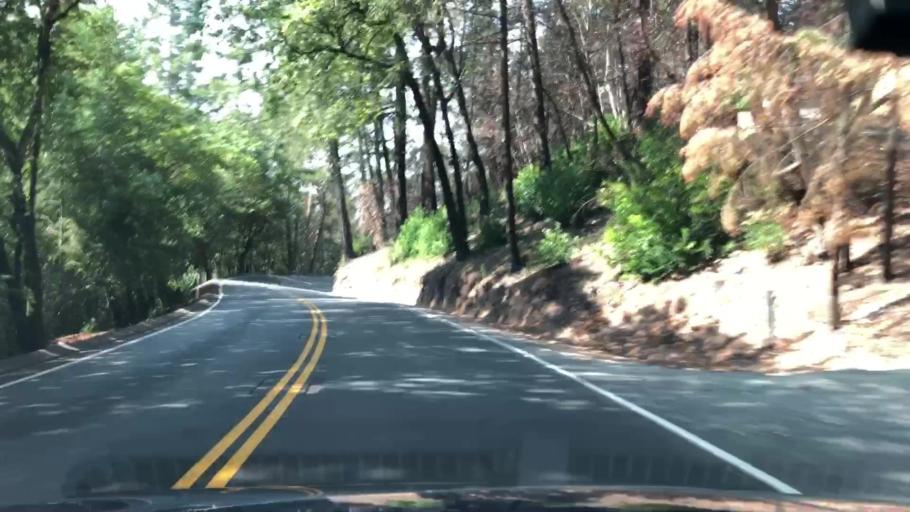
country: US
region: California
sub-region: Napa County
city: Calistoga
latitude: 38.6407
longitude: -122.5981
